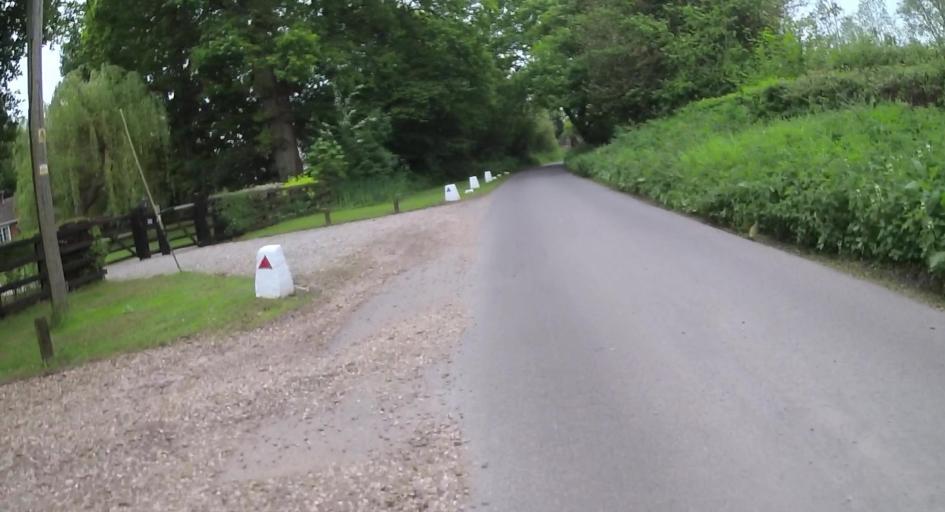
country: GB
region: England
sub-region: West Berkshire
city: Stratfield Mortimer
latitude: 51.3458
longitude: -1.0663
